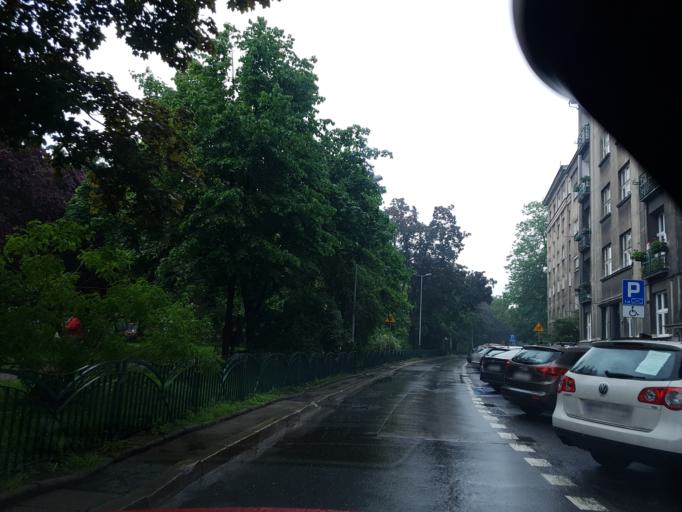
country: PL
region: Lesser Poland Voivodeship
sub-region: Krakow
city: Krakow
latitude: 50.0583
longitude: 19.9505
